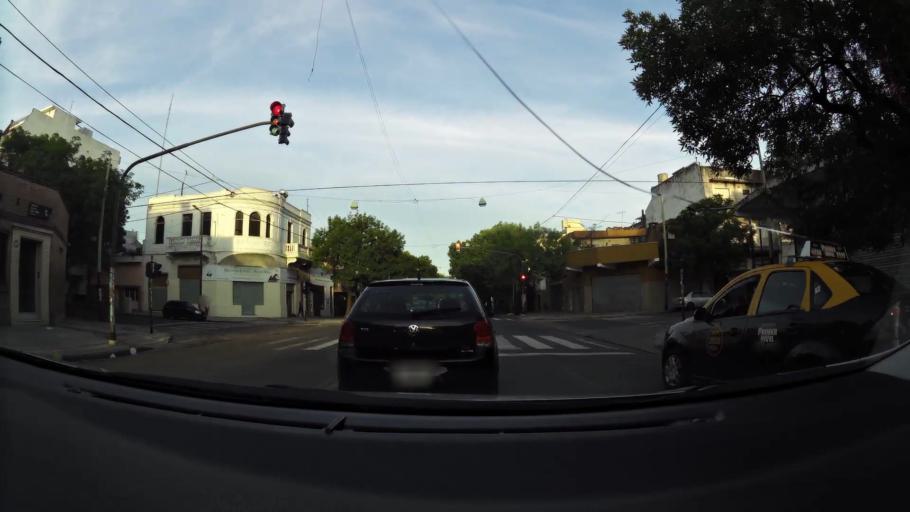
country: AR
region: Buenos Aires F.D.
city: Buenos Aires
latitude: -34.6398
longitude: -58.4212
